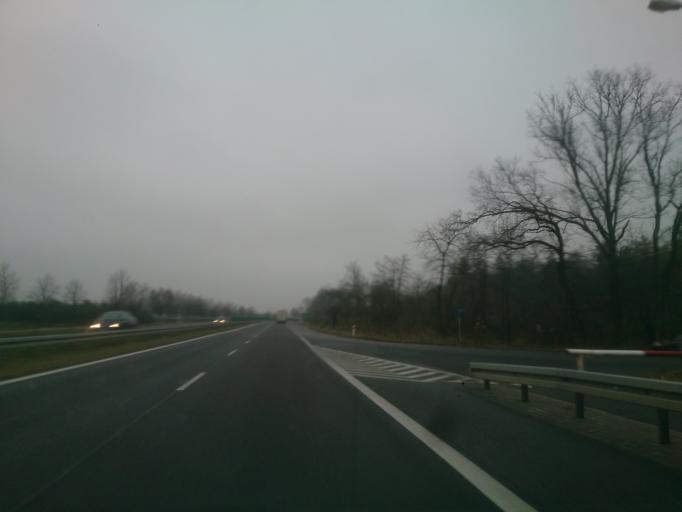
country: PL
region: Masovian Voivodeship
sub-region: Powiat plonski
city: Zaluski
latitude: 52.5030
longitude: 20.5361
